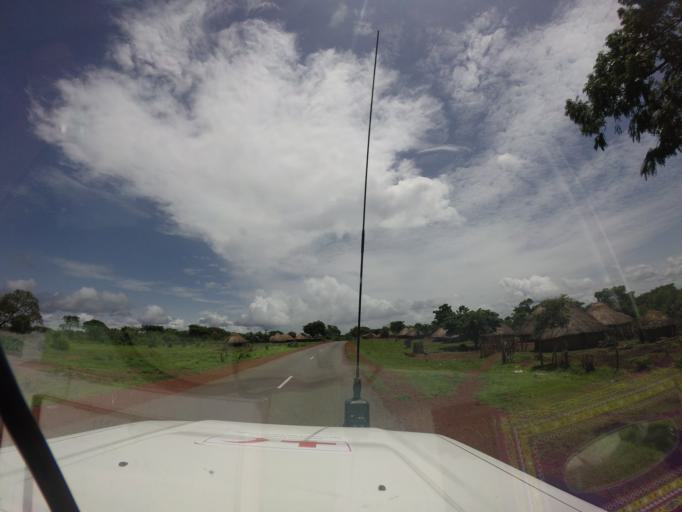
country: GN
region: Faranah
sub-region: Faranah Prefecture
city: Faranah
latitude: 10.0113
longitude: -10.8640
